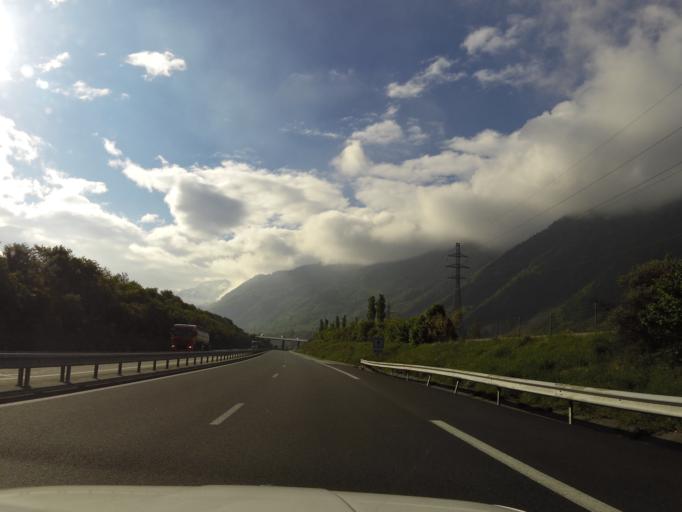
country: FR
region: Rhone-Alpes
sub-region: Departement de la Savoie
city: Villargondran
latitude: 45.2575
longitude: 6.3888
